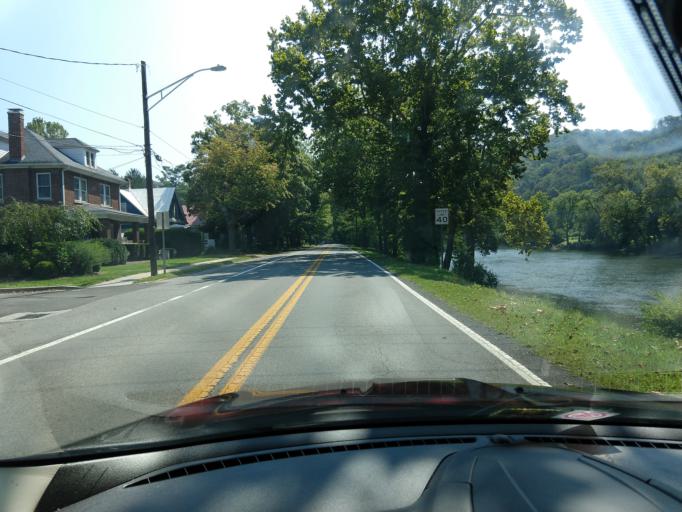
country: US
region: West Virginia
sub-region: Greenbrier County
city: Alderson
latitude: 37.7243
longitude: -80.6370
